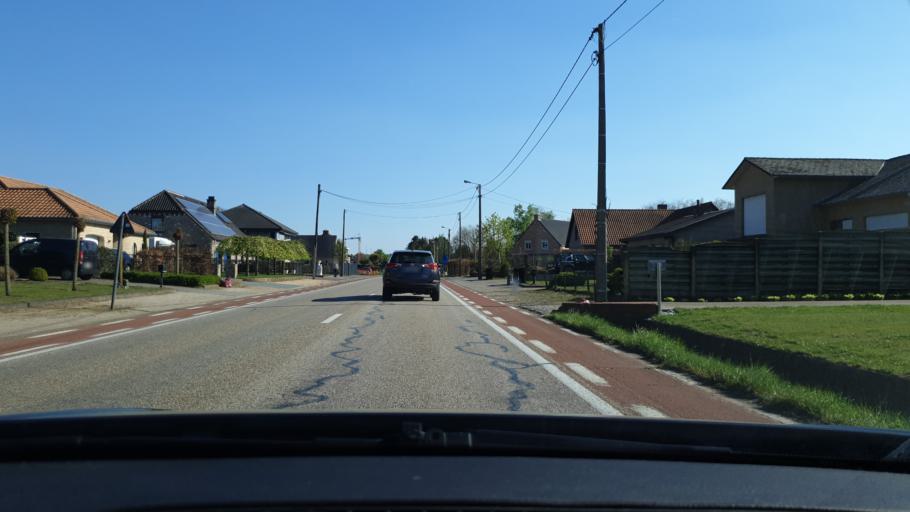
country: BE
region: Flanders
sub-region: Provincie Antwerpen
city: Laakdal
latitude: 51.0697
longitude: 5.0380
